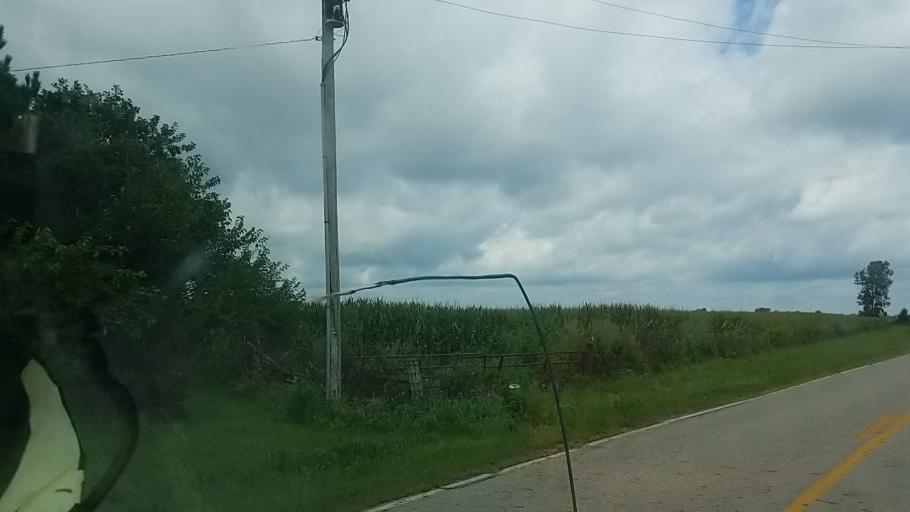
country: US
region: Ohio
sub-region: Madison County
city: Mount Sterling
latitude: 39.7910
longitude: -83.2286
